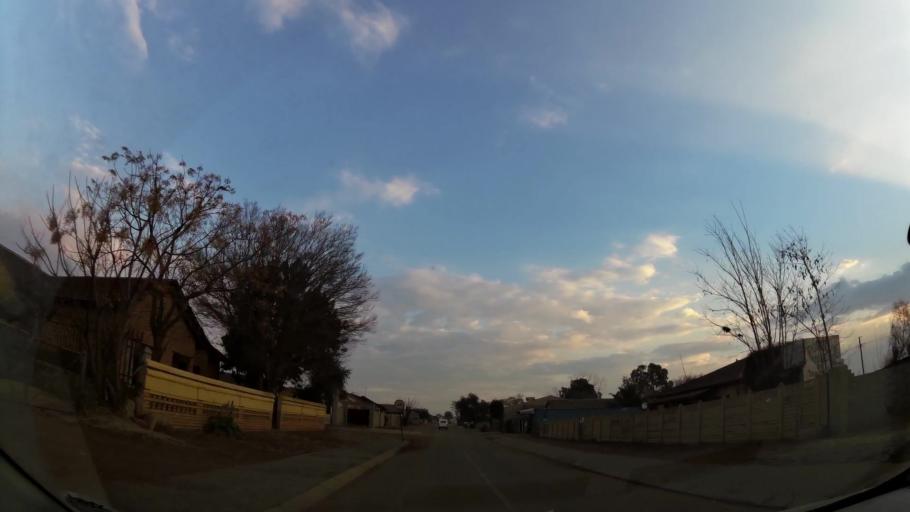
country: ZA
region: Gauteng
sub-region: City of Johannesburg Metropolitan Municipality
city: Orange Farm
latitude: -26.5450
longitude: 27.8849
